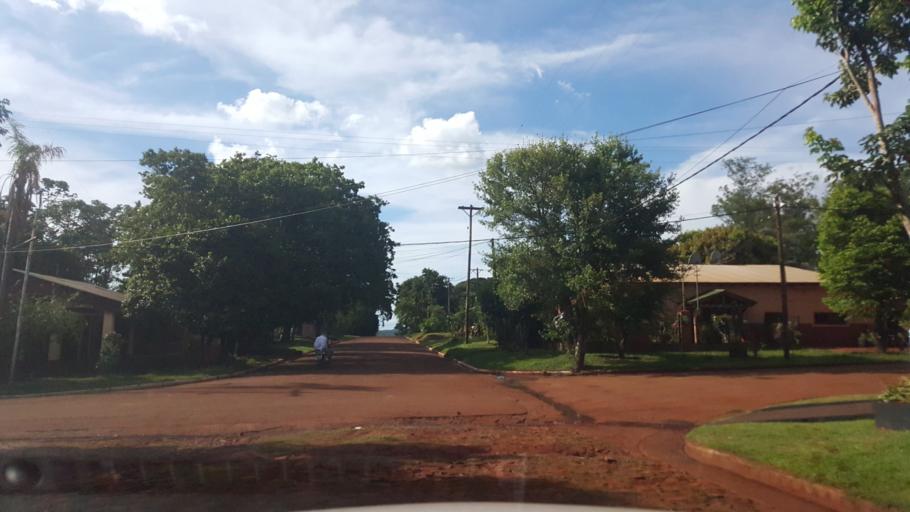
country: AR
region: Misiones
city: Santa Ana
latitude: -27.3697
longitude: -55.5797
